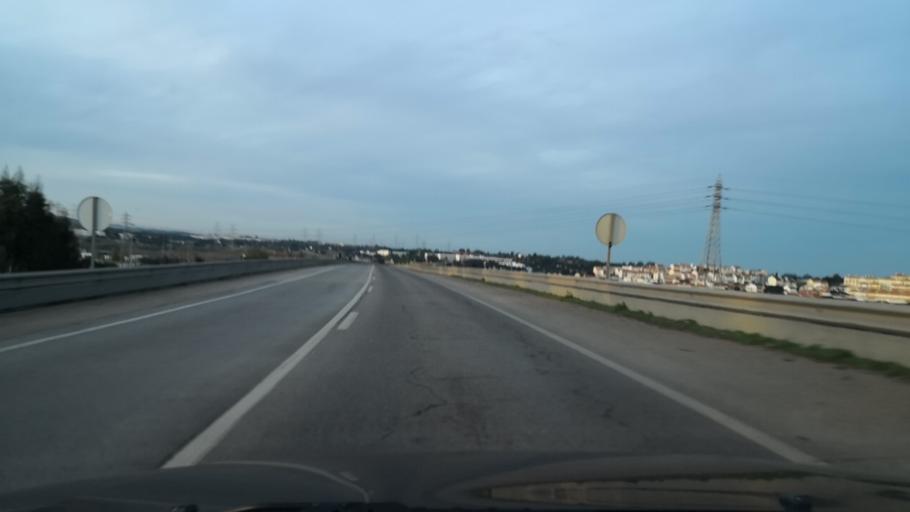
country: PT
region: Setubal
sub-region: Setubal
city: Setubal
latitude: 38.5101
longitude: -8.8378
